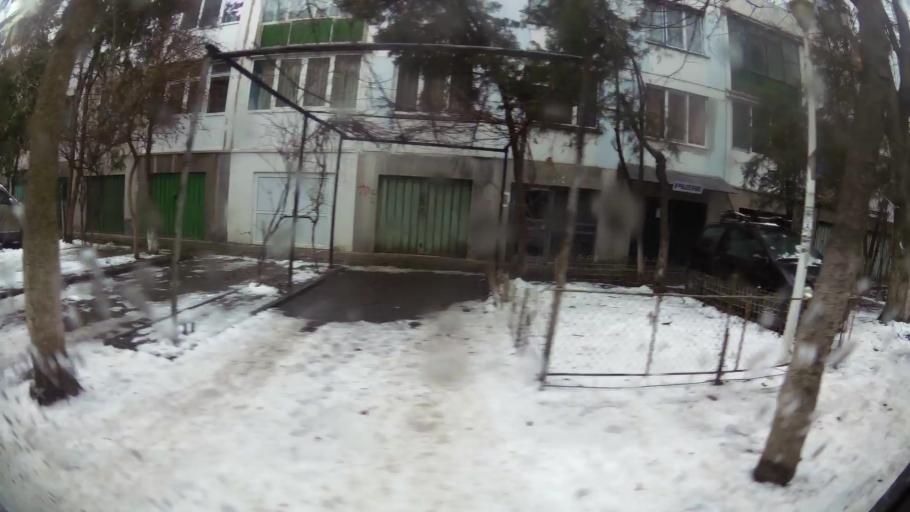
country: RO
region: Ilfov
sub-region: Comuna Chiajna
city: Rosu
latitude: 44.4130
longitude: 26.0164
